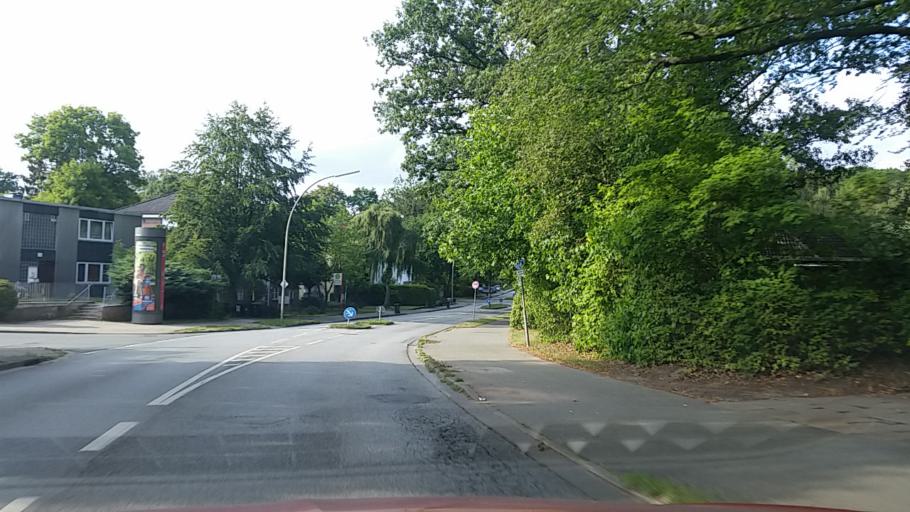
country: DE
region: Hamburg
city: Harburg
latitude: 53.4453
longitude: 9.9693
